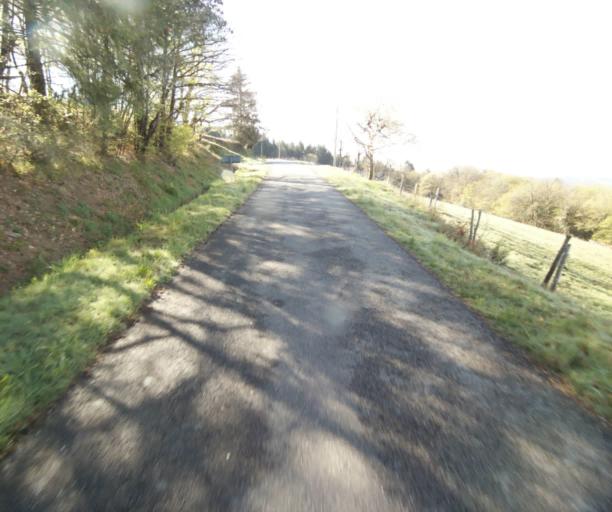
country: FR
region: Limousin
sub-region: Departement de la Correze
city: Laguenne
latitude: 45.2592
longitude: 1.8530
